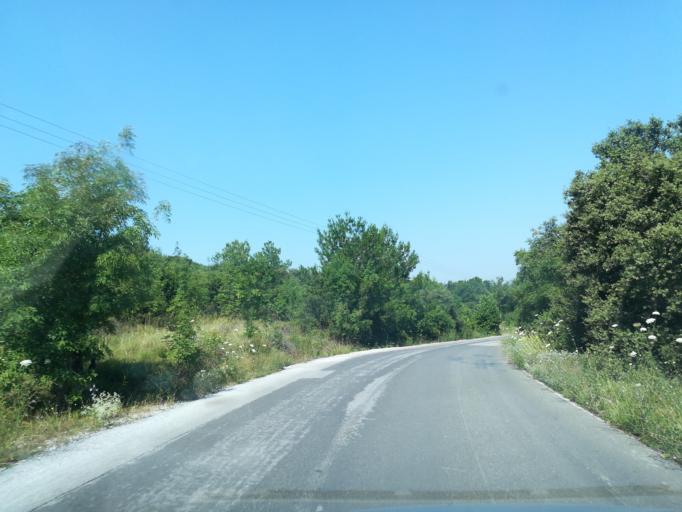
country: GR
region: Central Macedonia
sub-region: Nomos Thessalonikis
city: Asvestochori
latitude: 40.6298
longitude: 23.0334
